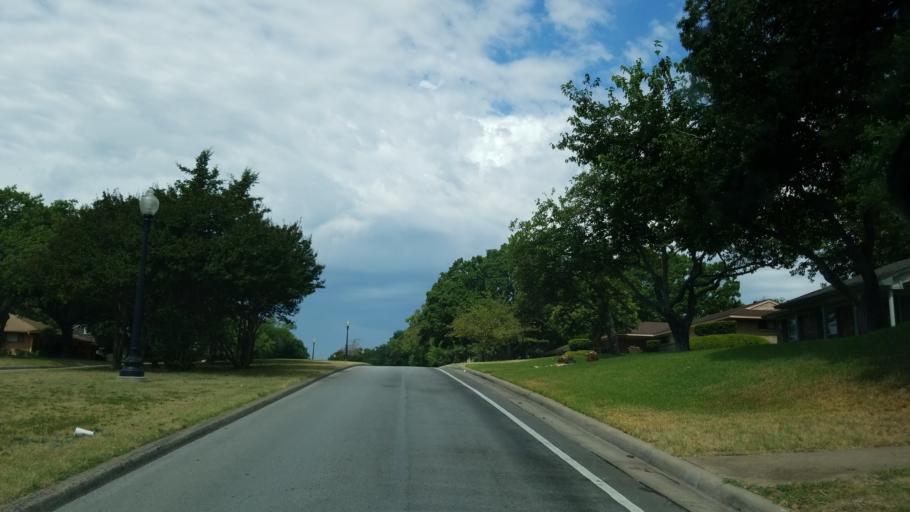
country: US
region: Texas
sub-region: Dallas County
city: Duncanville
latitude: 32.6729
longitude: -96.8422
